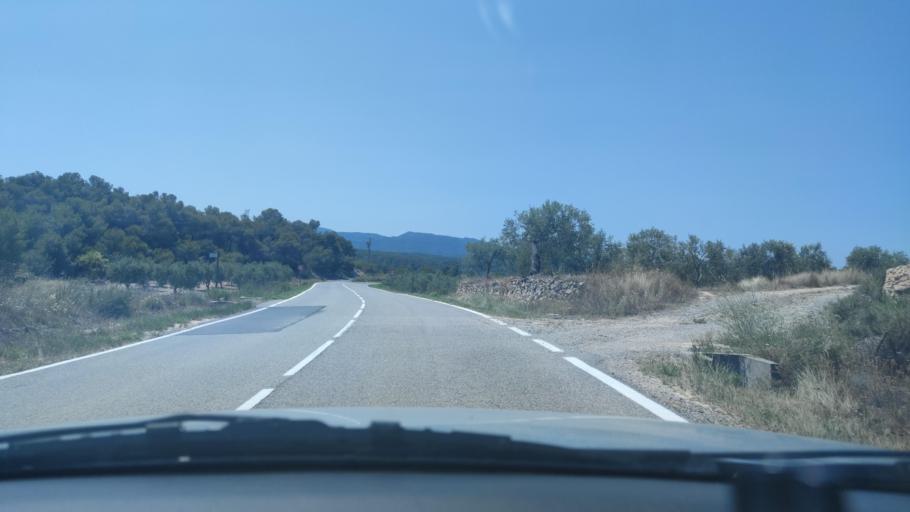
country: ES
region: Catalonia
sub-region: Provincia de Lleida
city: Vinaixa
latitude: 41.4201
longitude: 1.0149
